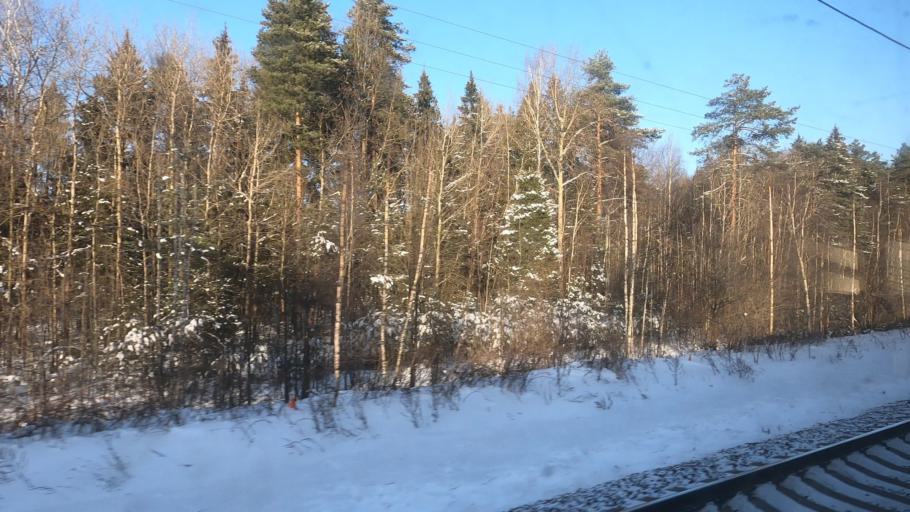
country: RU
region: Moskovskaya
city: Fryazevo
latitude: 55.7207
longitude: 38.4121
